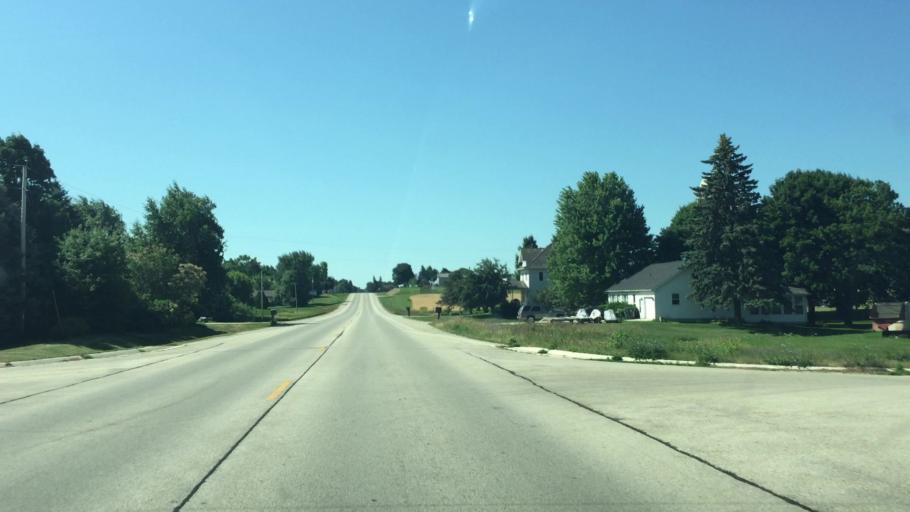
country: US
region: Wisconsin
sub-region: Calumet County
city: Chilton
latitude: 44.0514
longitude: -88.1630
